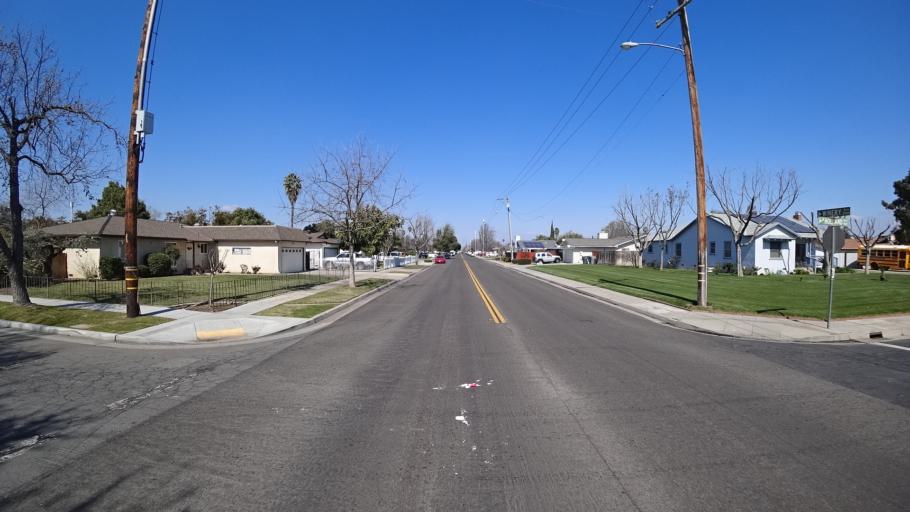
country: US
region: California
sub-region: Fresno County
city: Tarpey Village
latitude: 36.7976
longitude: -119.7318
